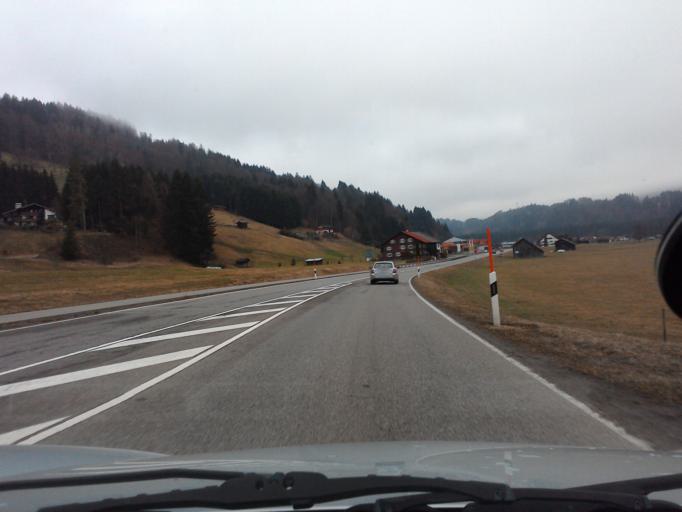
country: DE
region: Bavaria
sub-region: Swabia
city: Oberstdorf
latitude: 47.4294
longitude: 10.2673
